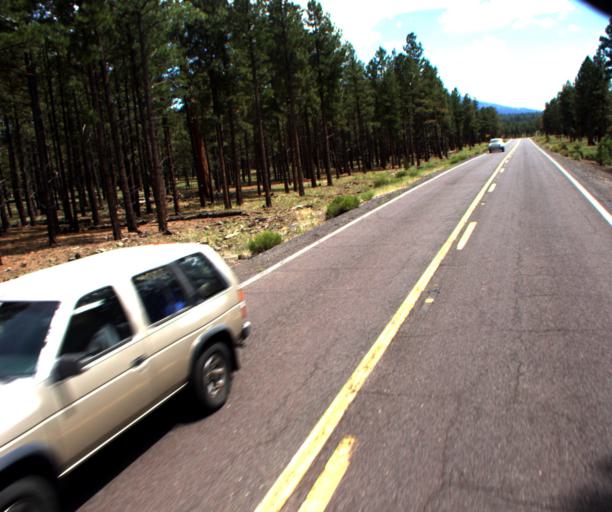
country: US
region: Arizona
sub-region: Coconino County
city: Parks
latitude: 35.4552
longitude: -111.7754
